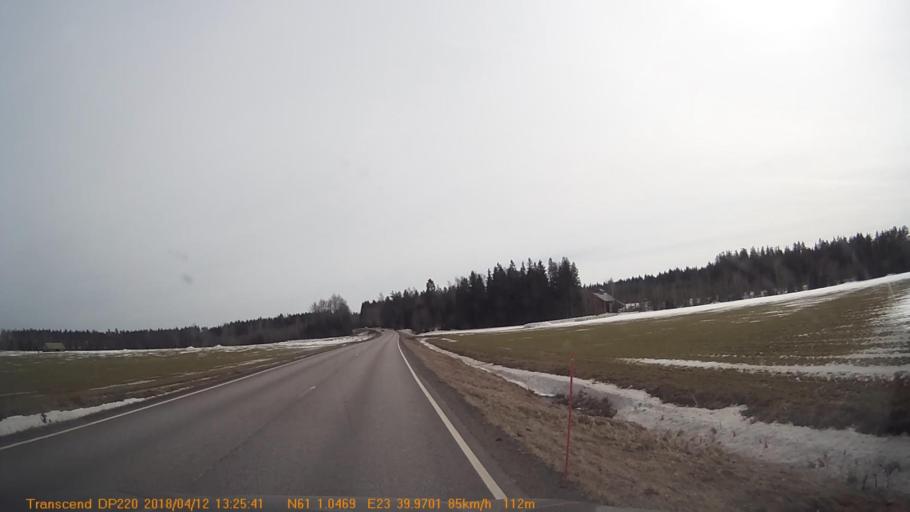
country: FI
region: Pirkanmaa
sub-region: Etelae-Pirkanmaa
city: Kylmaekoski
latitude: 61.0173
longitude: 23.6664
